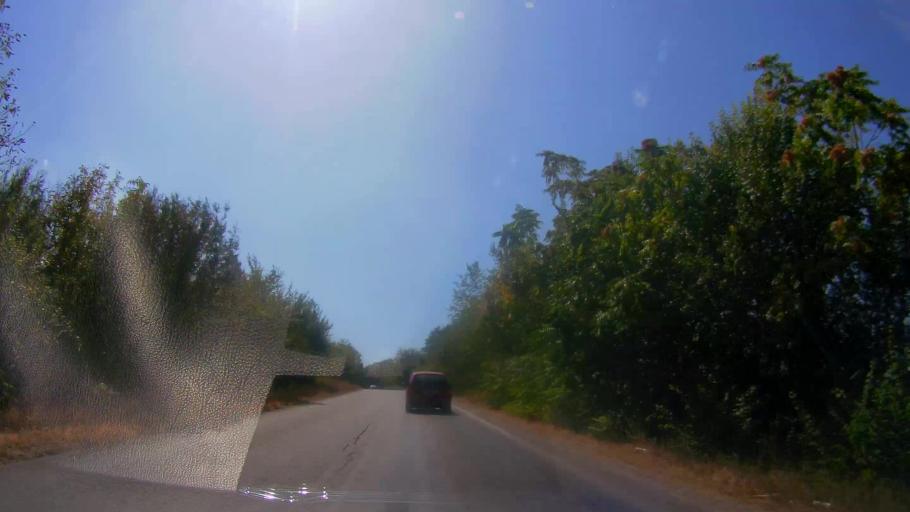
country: BG
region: Veliko Turnovo
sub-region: Obshtina Gorna Oryakhovitsa
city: Purvomaytsi
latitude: 43.2575
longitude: 25.6423
